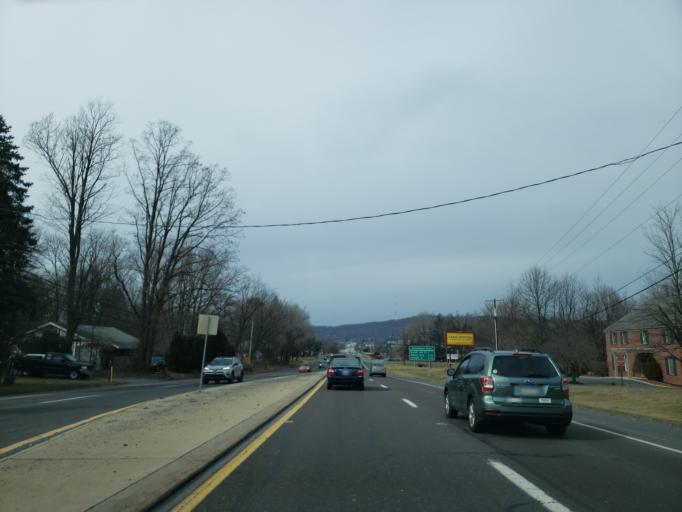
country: US
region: Pennsylvania
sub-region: Lehigh County
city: Coopersburg
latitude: 40.5406
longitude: -75.4142
